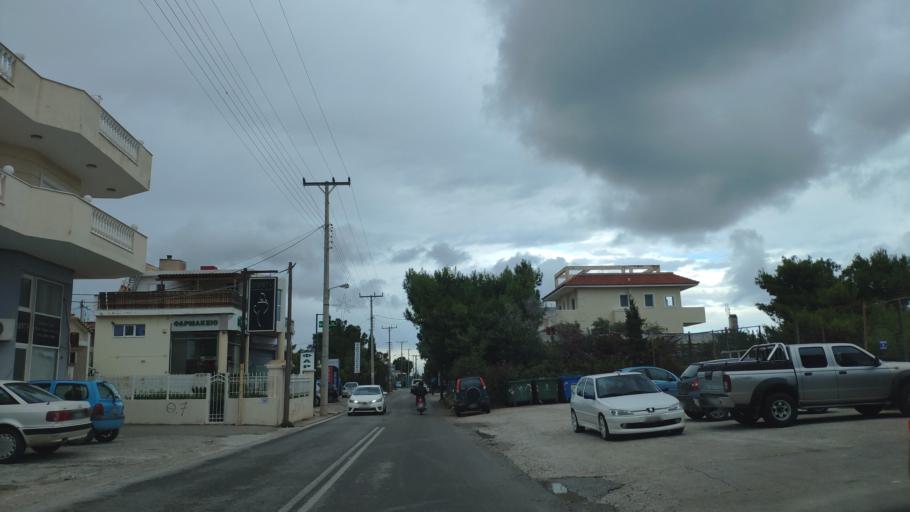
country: GR
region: Attica
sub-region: Nomarchia Anatolikis Attikis
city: Artemida
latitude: 37.9608
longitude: 24.0056
